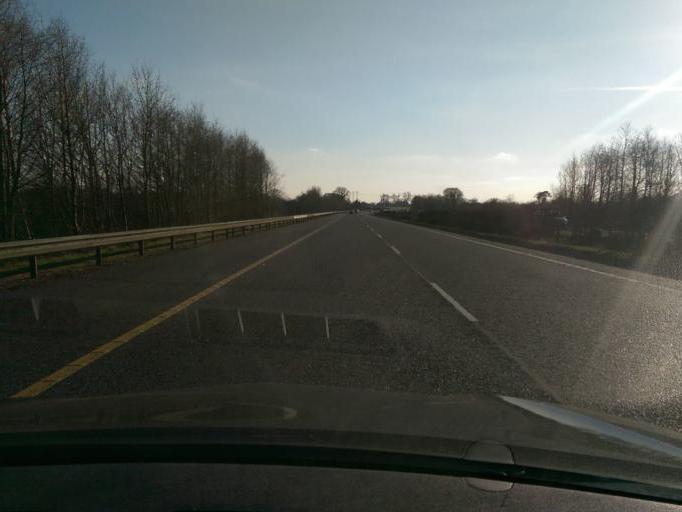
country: IE
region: Leinster
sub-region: Laois
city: Portlaoise
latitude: 53.0227
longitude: -7.2599
